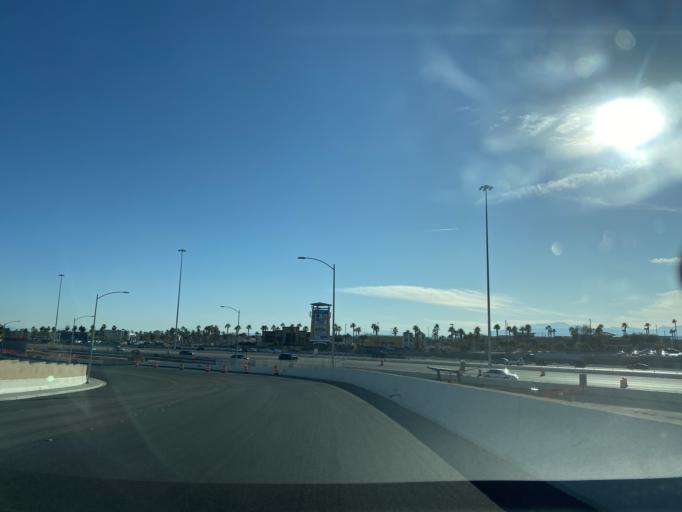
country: US
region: Nevada
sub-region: Clark County
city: Las Vegas
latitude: 36.2727
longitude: -115.2612
